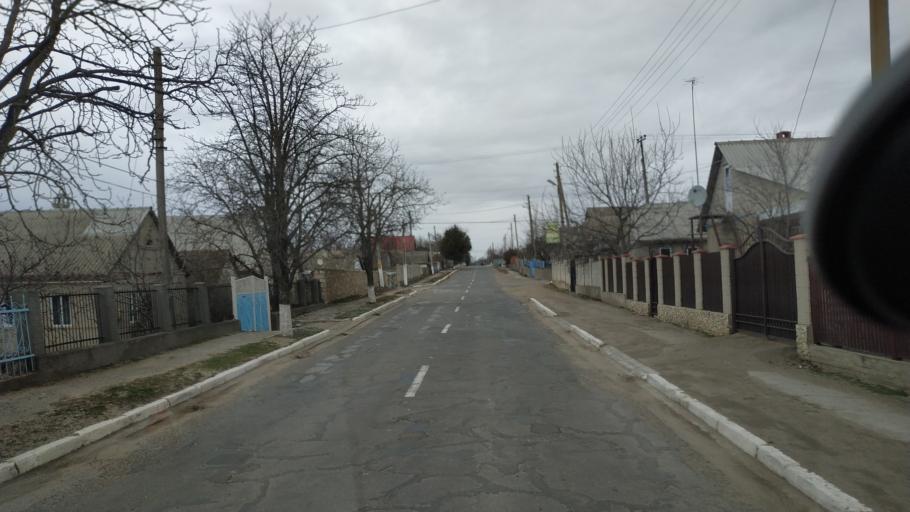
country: MD
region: Telenesti
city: Cocieri
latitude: 47.3004
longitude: 29.1142
